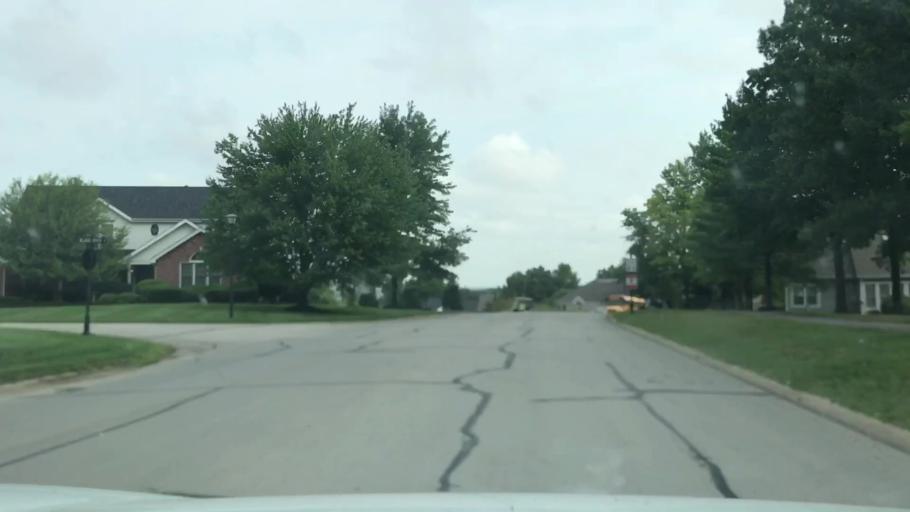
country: US
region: Missouri
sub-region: Saint Charles County
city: Cottleville
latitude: 38.7155
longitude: -90.6347
